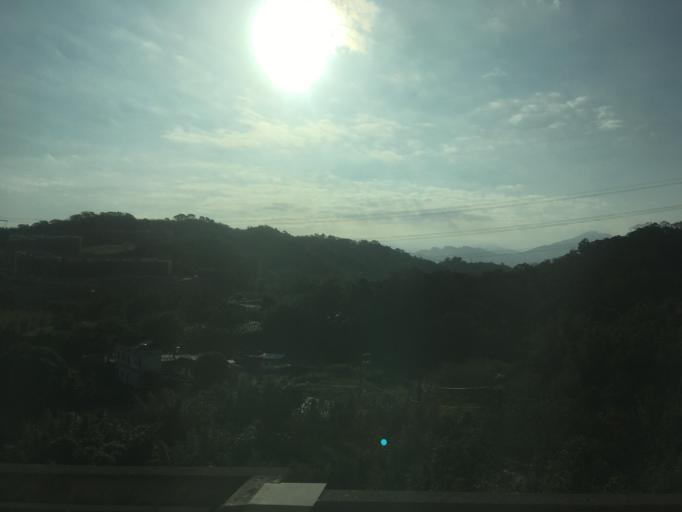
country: TW
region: Taiwan
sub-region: Hsinchu
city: Hsinchu
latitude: 24.7479
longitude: 121.0168
